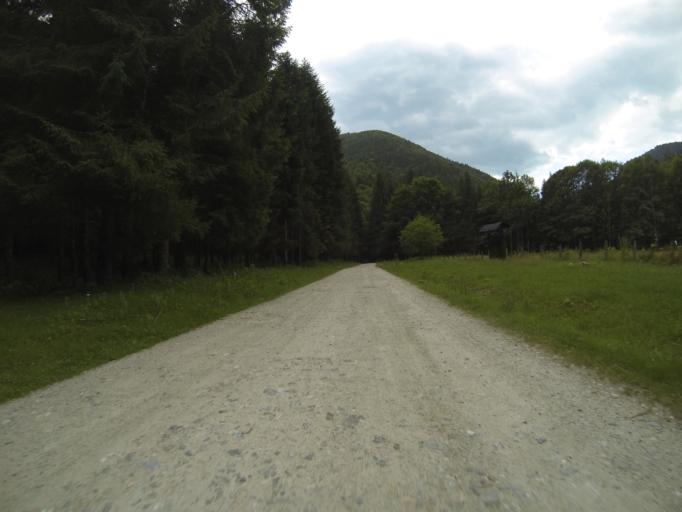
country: RO
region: Gorj
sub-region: Comuna Polovragi
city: Polovragi
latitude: 45.2583
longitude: 23.7689
